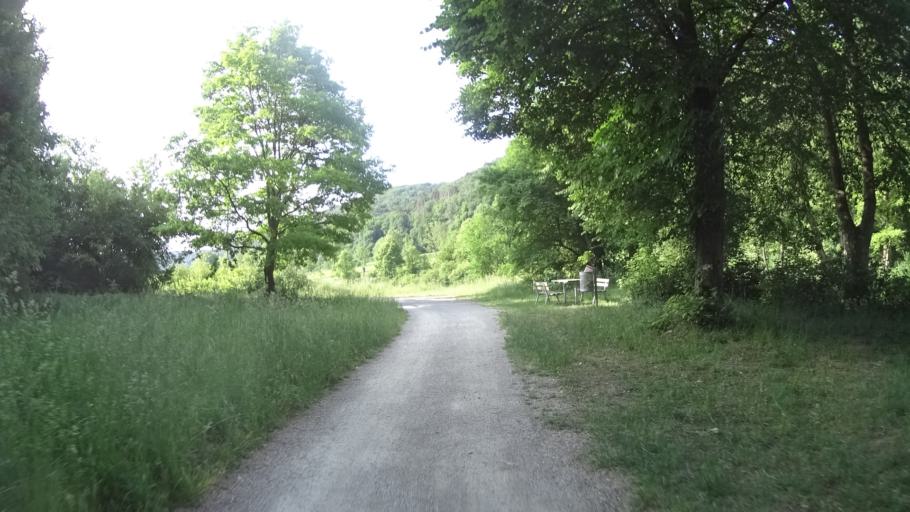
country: DE
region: Bavaria
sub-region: Lower Bavaria
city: Riedenburg
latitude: 48.9508
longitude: 11.7358
